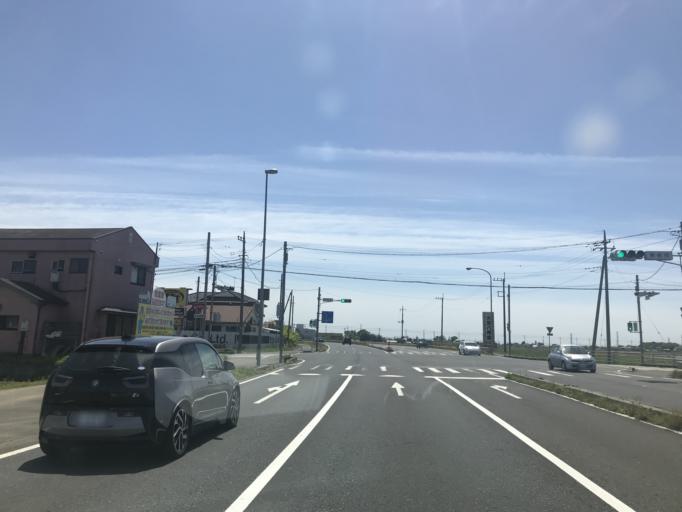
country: JP
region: Ibaraki
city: Ishige
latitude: 36.2028
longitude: 139.9842
